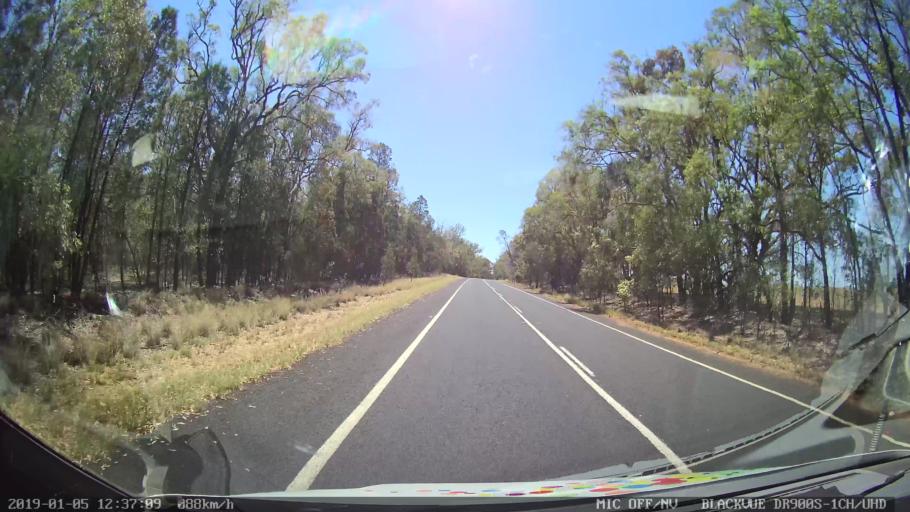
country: AU
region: New South Wales
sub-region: Warrumbungle Shire
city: Coonabarabran
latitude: -31.2047
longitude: 149.4507
